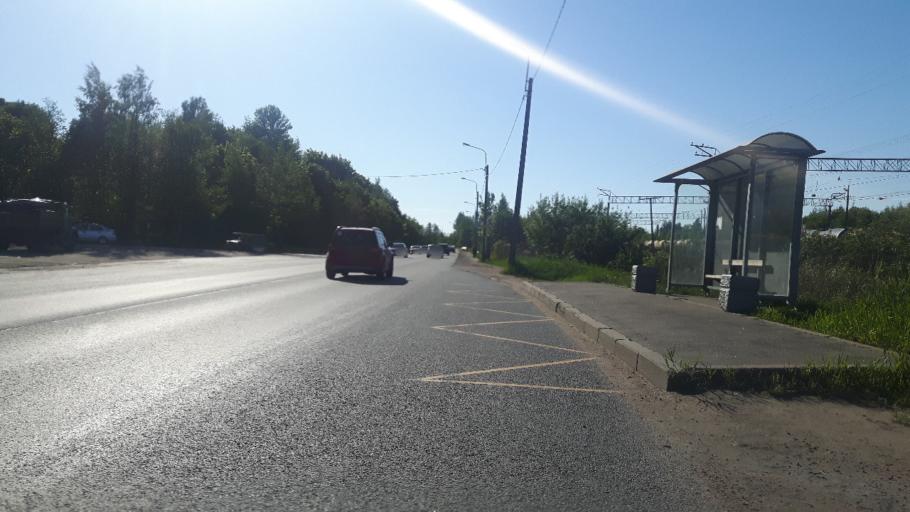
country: RU
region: St.-Petersburg
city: Bol'shaya Izhora
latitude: 59.9276
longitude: 29.6567
